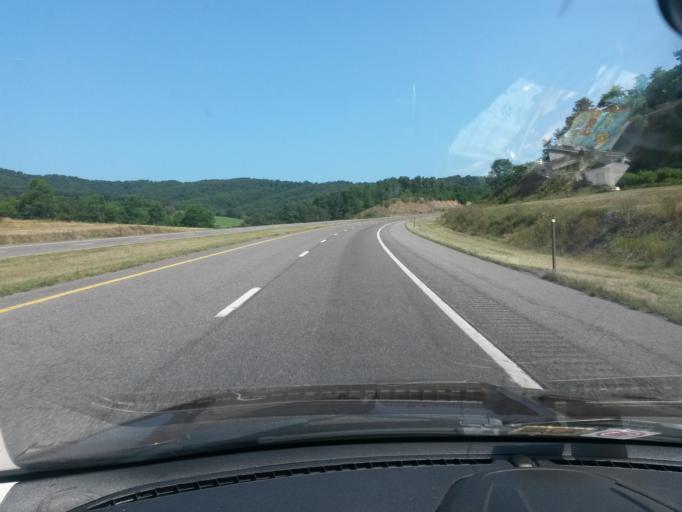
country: US
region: West Virginia
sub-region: Hardy County
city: Moorefield
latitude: 39.0721
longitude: -78.8035
